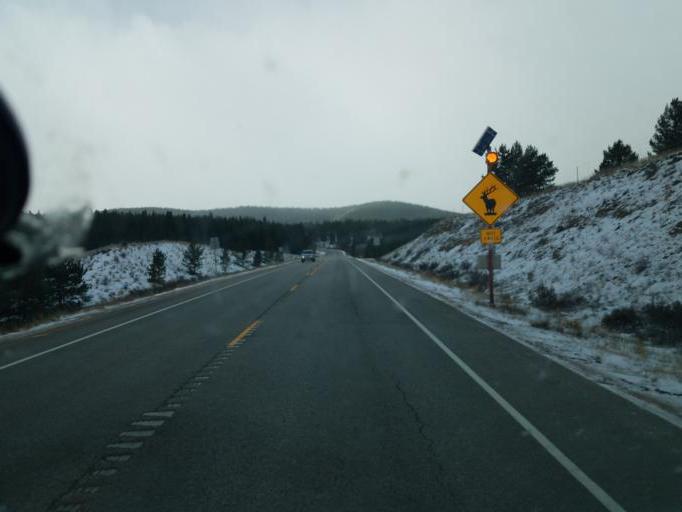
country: US
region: Colorado
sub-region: Clear Creek County
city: Georgetown
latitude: 39.4337
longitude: -105.7583
